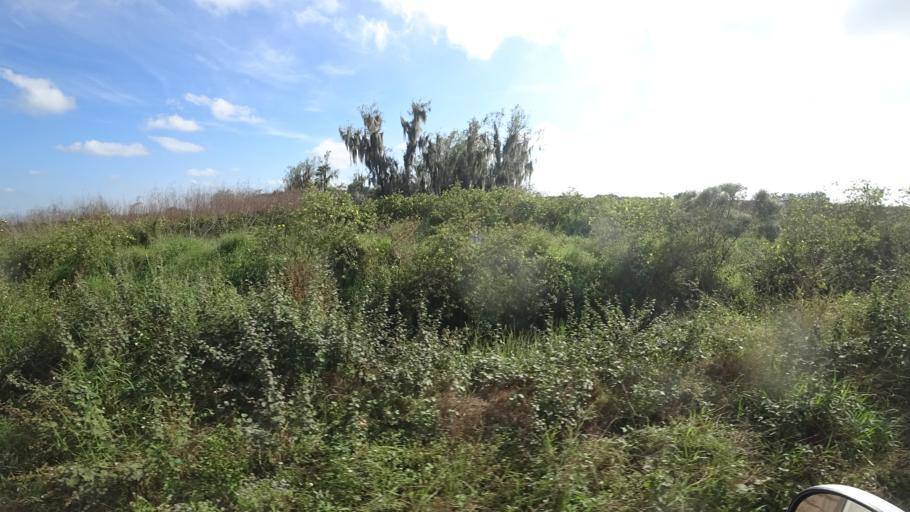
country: US
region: Florida
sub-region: DeSoto County
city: Arcadia
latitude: 27.3463
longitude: -82.1103
